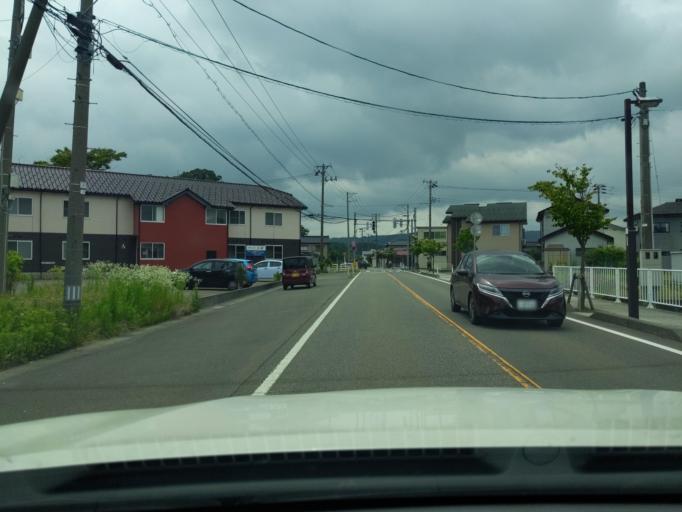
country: JP
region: Niigata
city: Kashiwazaki
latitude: 37.3406
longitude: 138.5698
